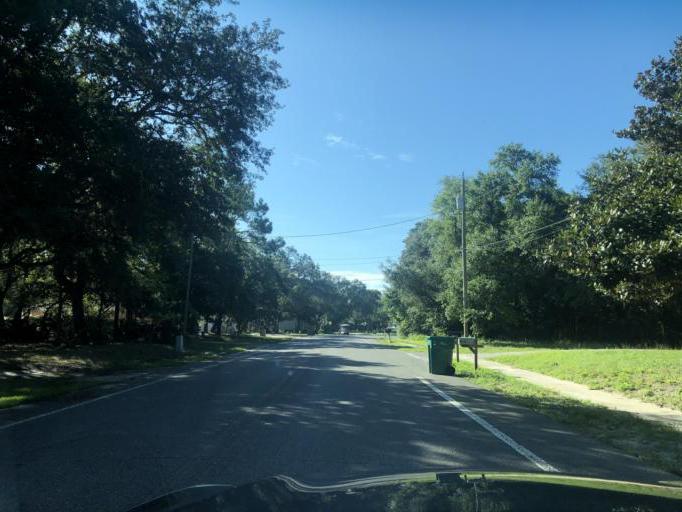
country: US
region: Florida
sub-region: Okaloosa County
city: Destin
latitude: 30.4069
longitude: -86.4994
